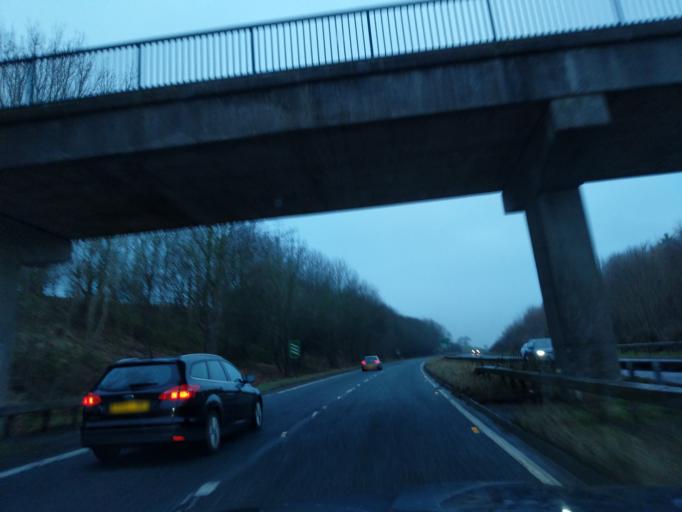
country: GB
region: England
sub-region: Northumberland
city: Morpeth
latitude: 55.1683
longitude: -1.7246
